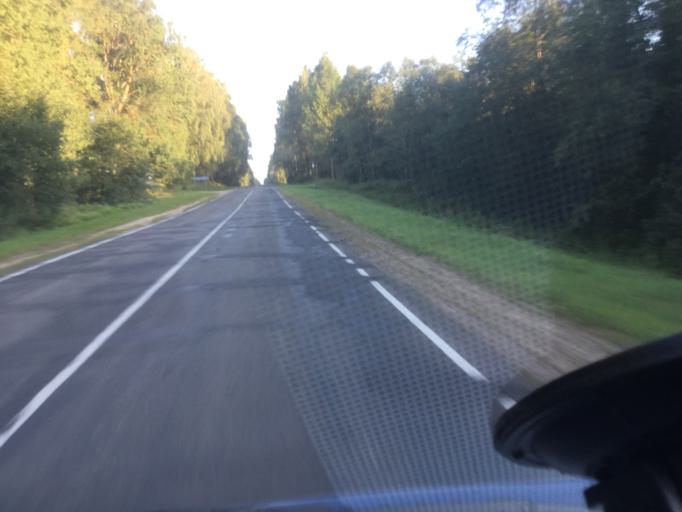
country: BY
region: Vitebsk
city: Navapolatsk
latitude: 55.6451
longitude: 28.6245
